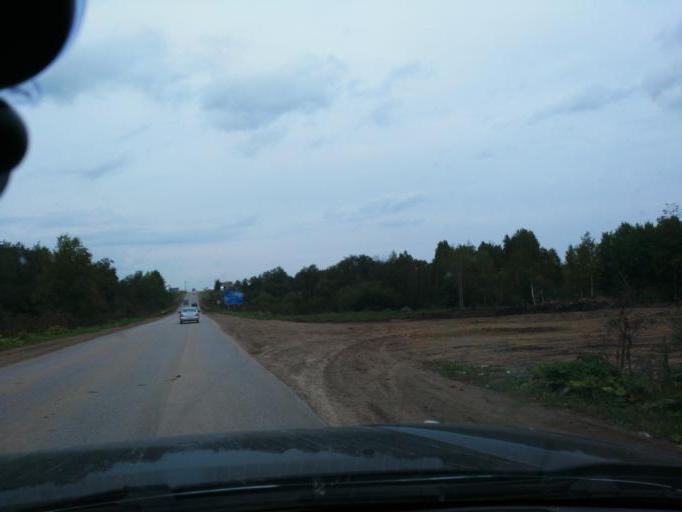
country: RU
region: Perm
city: Chernushka
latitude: 56.5408
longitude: 56.1006
